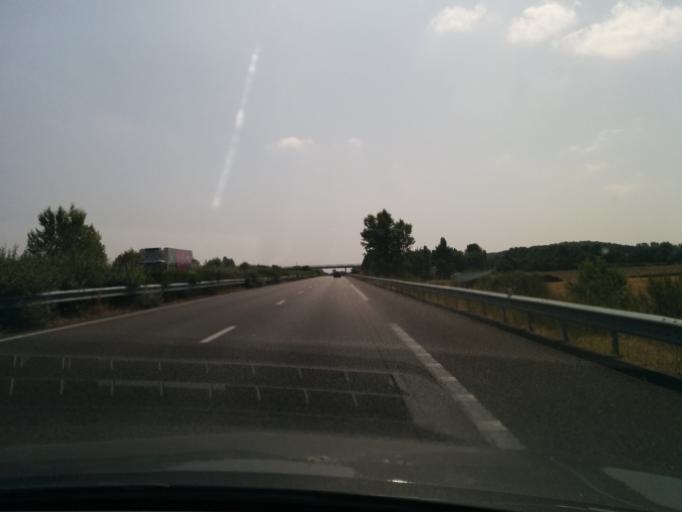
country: FR
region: Midi-Pyrenees
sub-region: Departement du Tarn
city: Saint-Sulpice-la-Pointe
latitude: 43.7541
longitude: 1.6821
